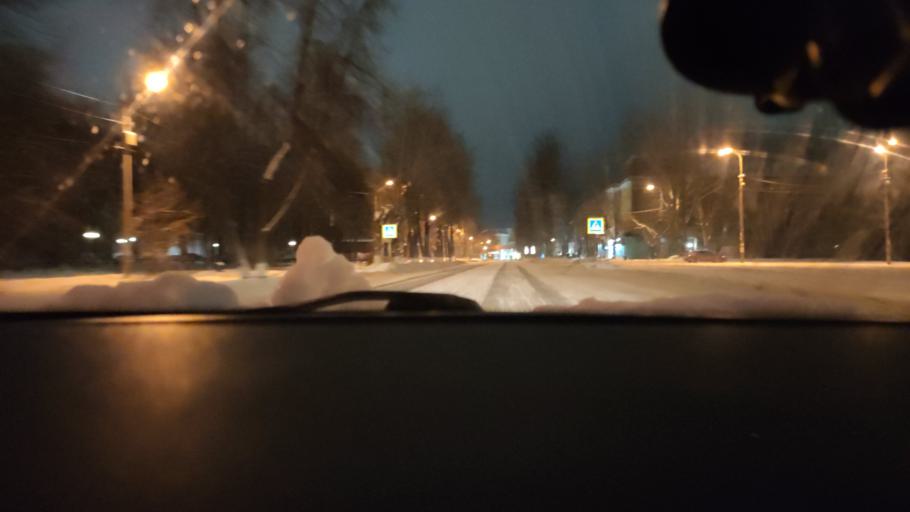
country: RU
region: Perm
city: Krasnokamsk
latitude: 58.0797
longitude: 55.7506
